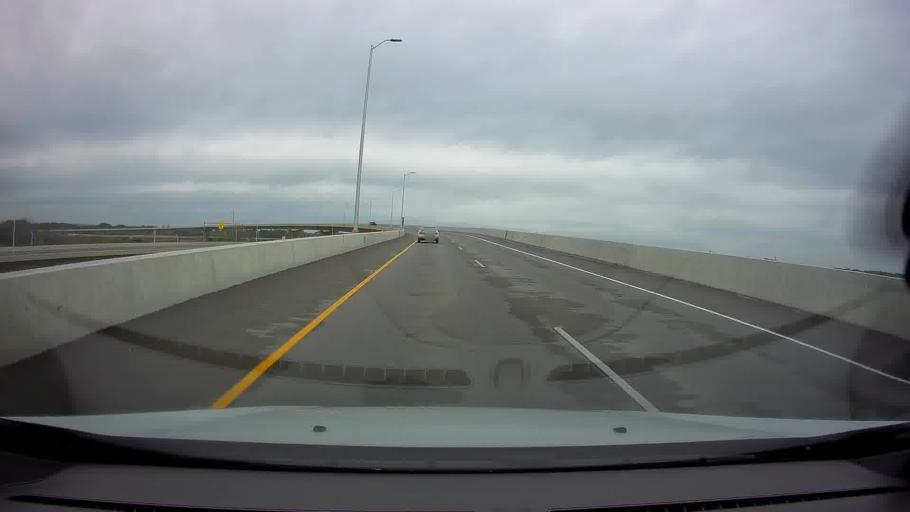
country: US
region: Wisconsin
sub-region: Brown County
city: Howard
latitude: 44.5586
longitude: -88.0481
